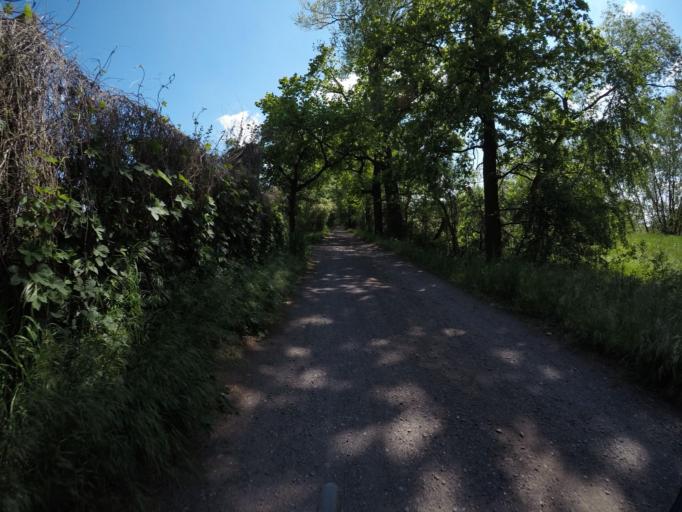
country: DE
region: Brandenburg
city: Werder
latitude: 52.4095
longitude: 12.9467
